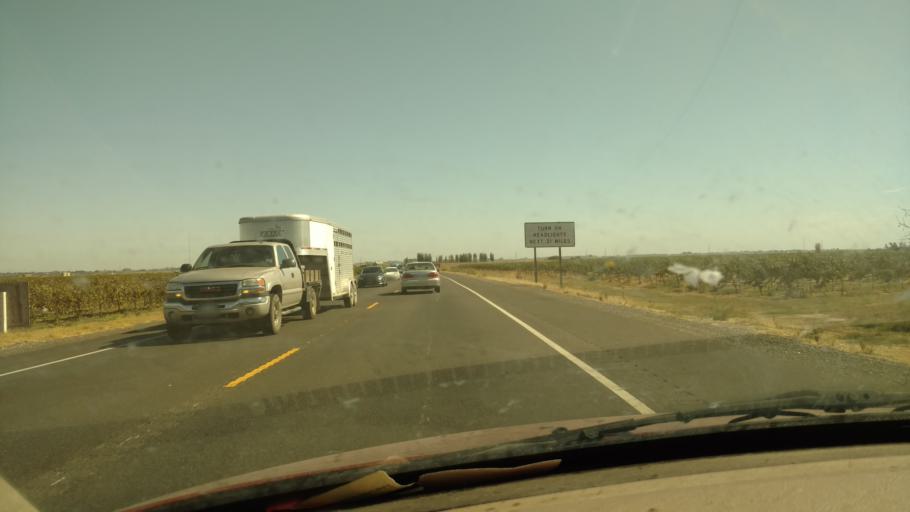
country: US
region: California
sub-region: Solano County
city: Rio Vista
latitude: 38.1535
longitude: -121.6725
